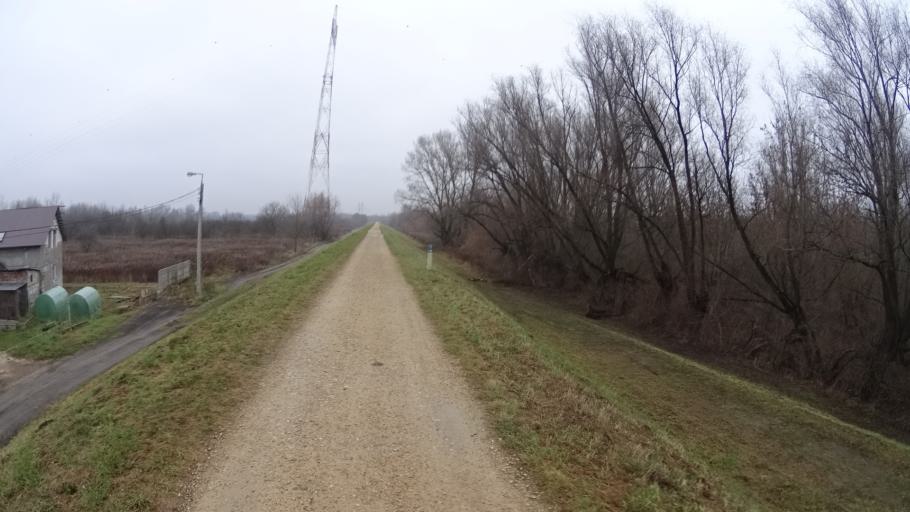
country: PL
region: Masovian Voivodeship
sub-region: Warszawa
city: Wilanow
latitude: 52.1968
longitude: 21.1001
